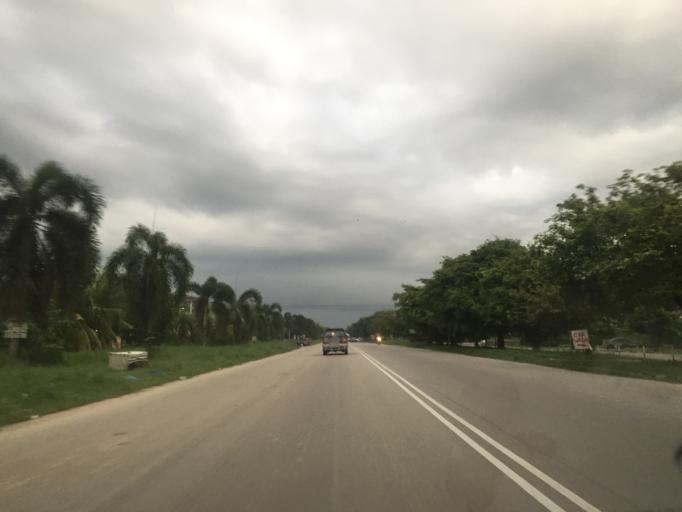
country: MY
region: Penang
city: Tasek Glugor
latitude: 5.5151
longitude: 100.5400
